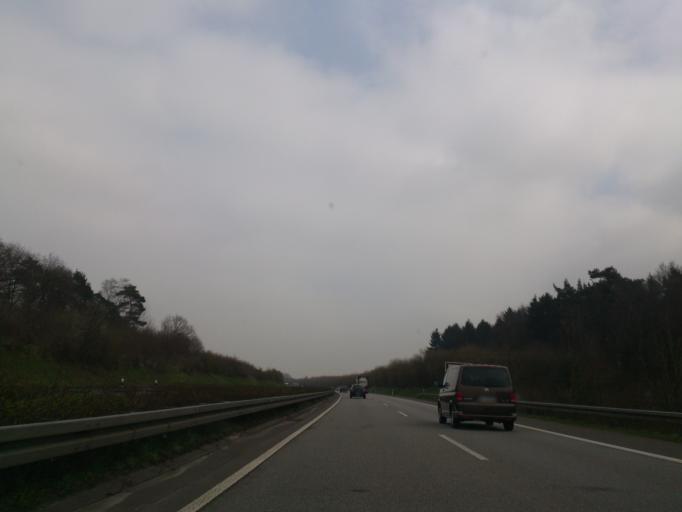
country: DE
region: North Rhine-Westphalia
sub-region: Regierungsbezirk Dusseldorf
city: Bruggen
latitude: 51.2037
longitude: 6.1738
